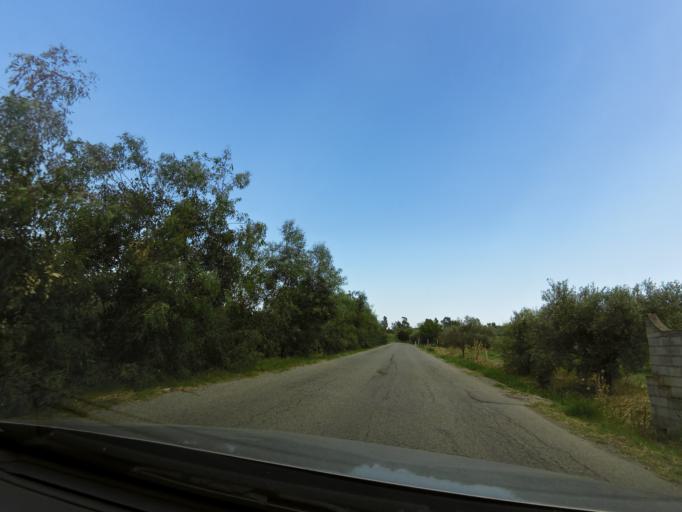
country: IT
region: Calabria
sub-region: Provincia di Reggio Calabria
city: Monasterace Marina
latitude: 38.4227
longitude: 16.5494
